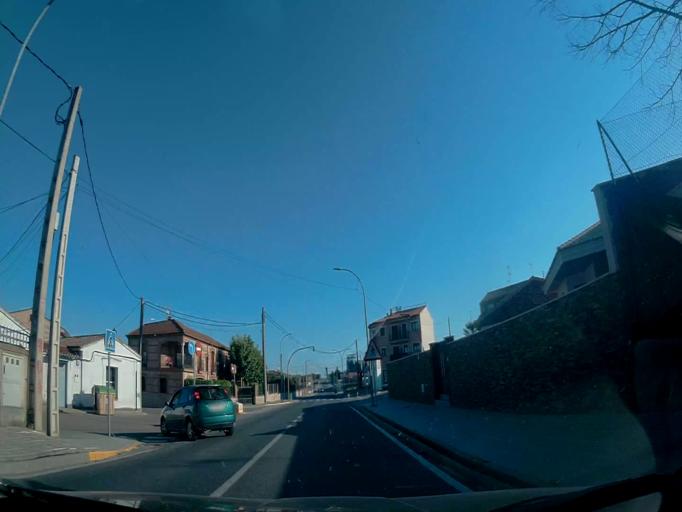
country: ES
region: Castille-La Mancha
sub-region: Province of Toledo
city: Almorox
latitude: 40.2306
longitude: -4.3921
